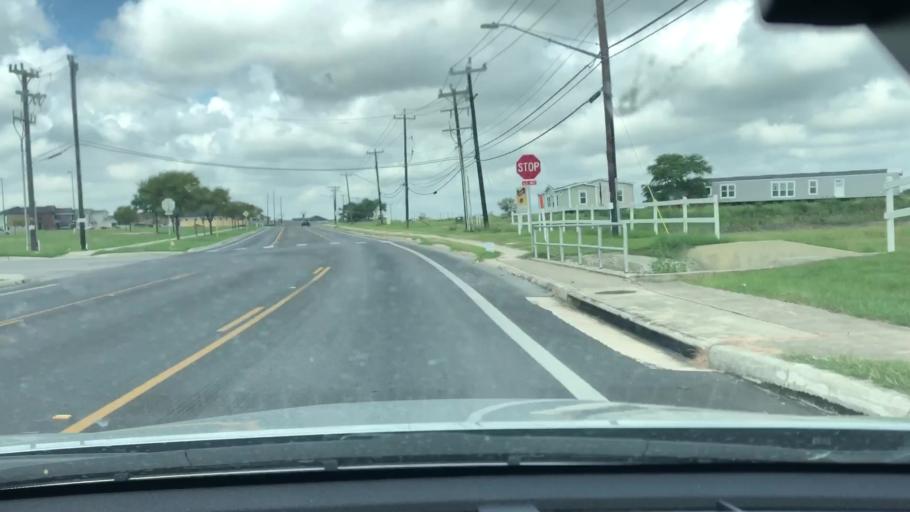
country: US
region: Texas
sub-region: Bexar County
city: Windcrest
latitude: 29.4968
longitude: -98.3625
